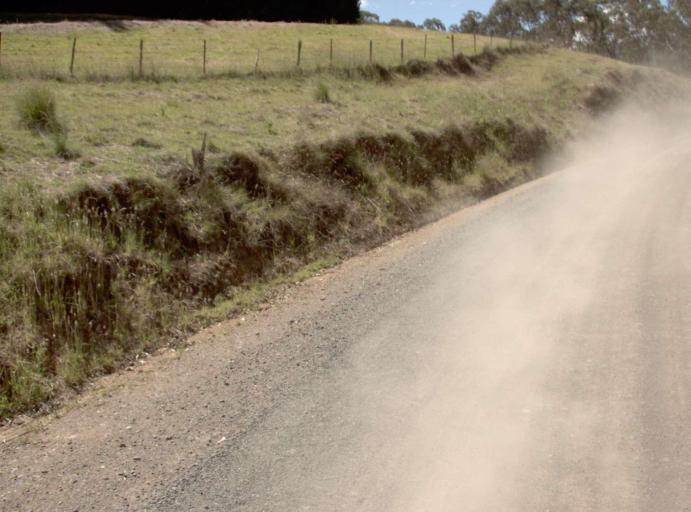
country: AU
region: New South Wales
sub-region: Bombala
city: Bombala
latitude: -37.1246
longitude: 148.6631
